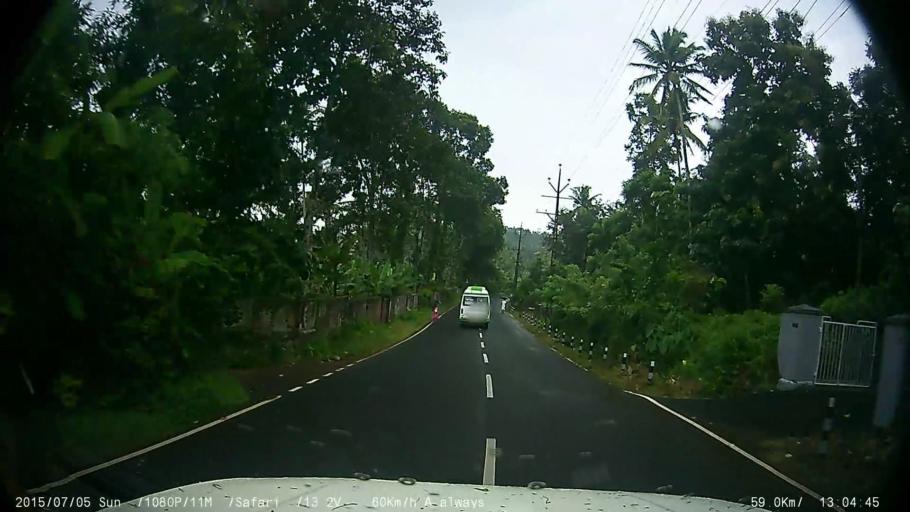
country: IN
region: Kerala
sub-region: Kottayam
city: Changanacheri
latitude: 9.5066
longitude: 76.5718
